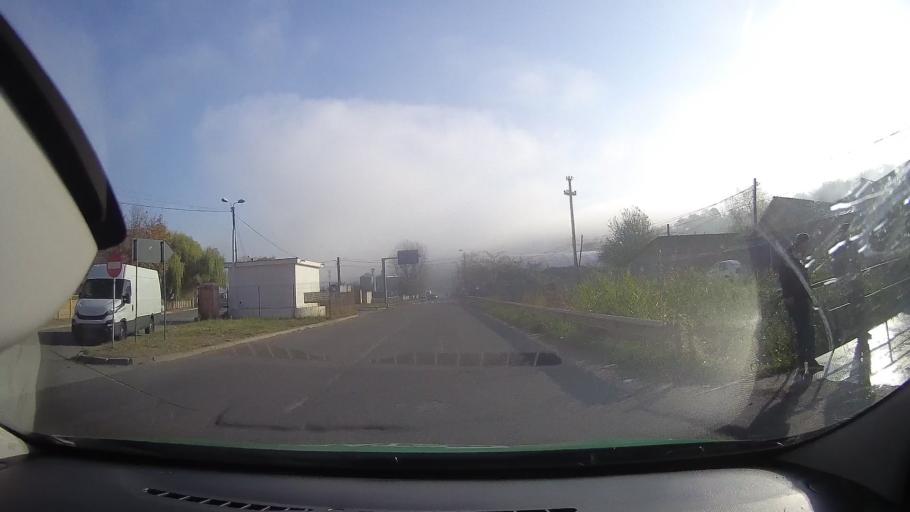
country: RO
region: Tulcea
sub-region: Municipiul Tulcea
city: Tulcea
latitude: 45.1656
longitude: 28.8207
